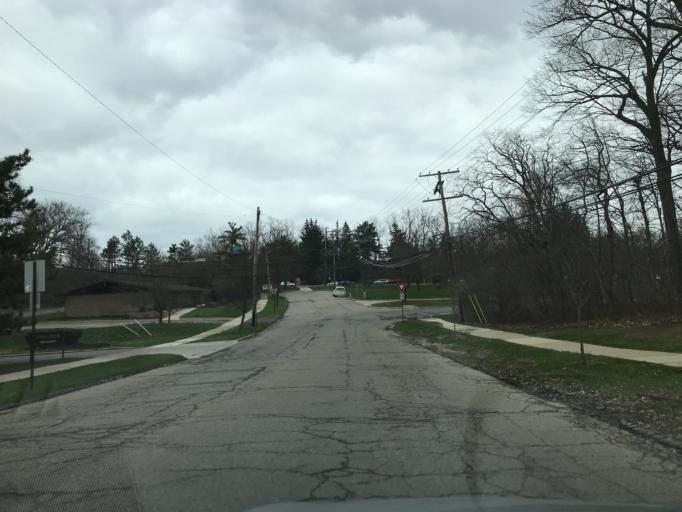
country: US
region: Michigan
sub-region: Washtenaw County
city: Ann Arbor
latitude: 42.2577
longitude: -83.7106
